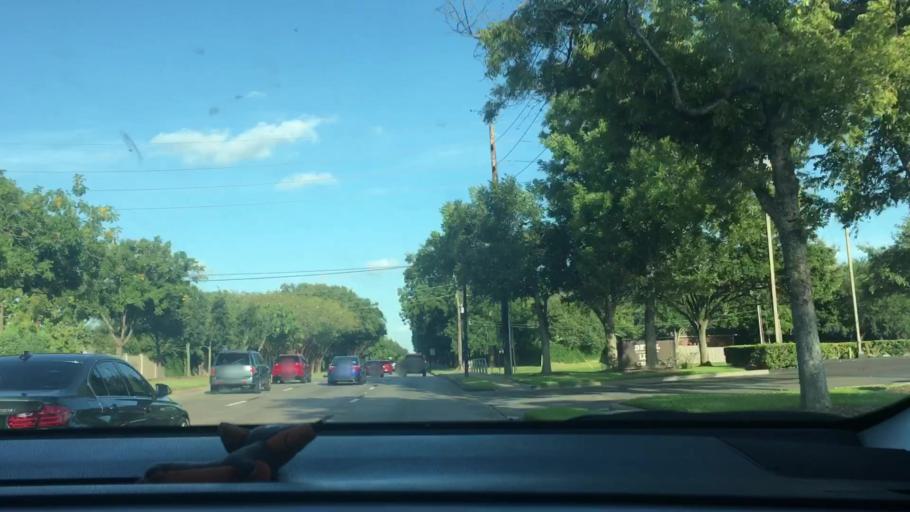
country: US
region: Texas
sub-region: Fort Bend County
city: Sugar Land
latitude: 29.5958
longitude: -95.6155
